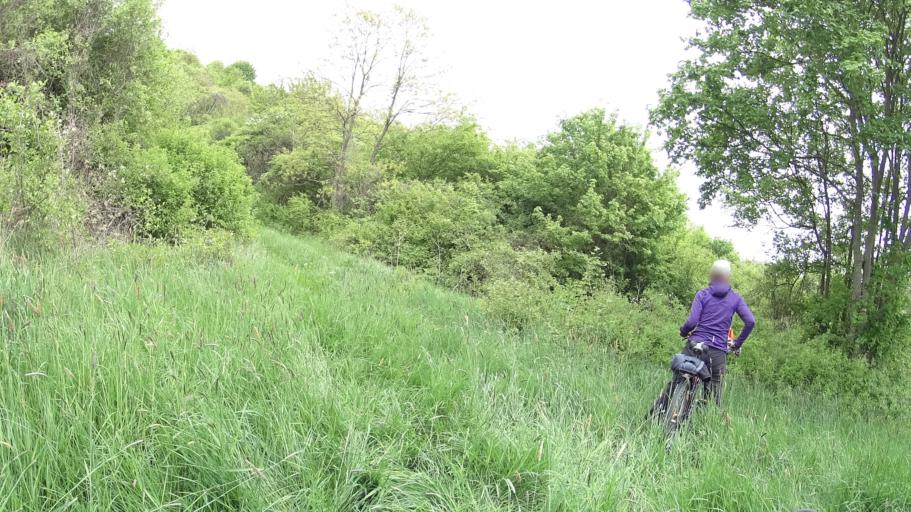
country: HU
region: Pest
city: Kosd
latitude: 47.8213
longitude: 19.2769
